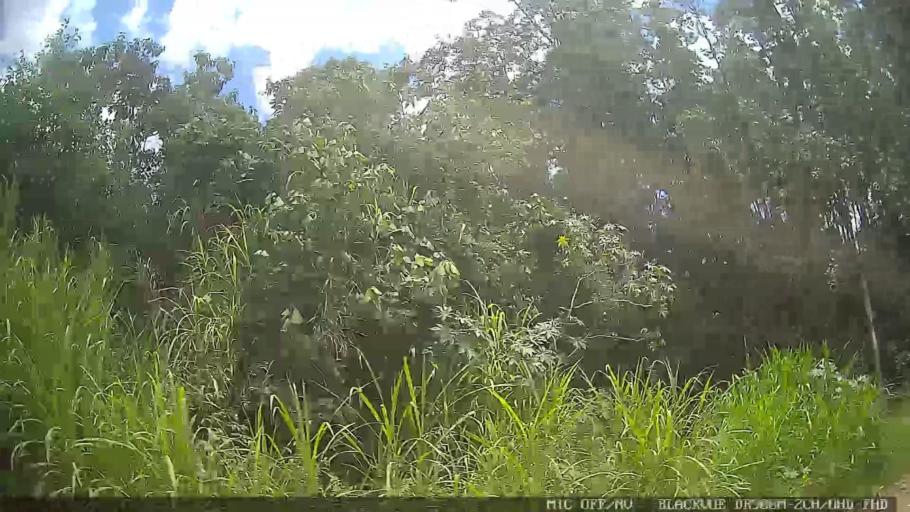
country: BR
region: Sao Paulo
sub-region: Atibaia
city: Atibaia
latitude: -23.1432
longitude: -46.6066
